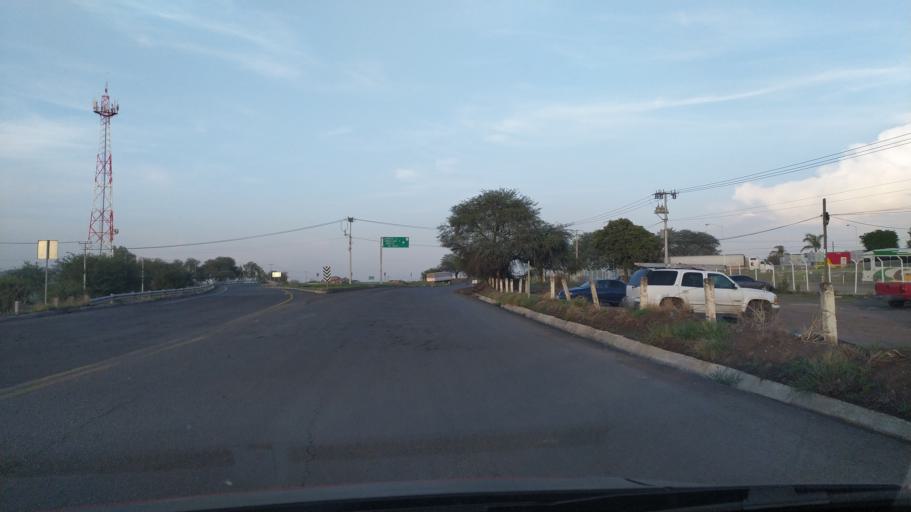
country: MX
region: Michoacan
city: Vistahermosa de Negrete
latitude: 20.2683
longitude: -102.4484
